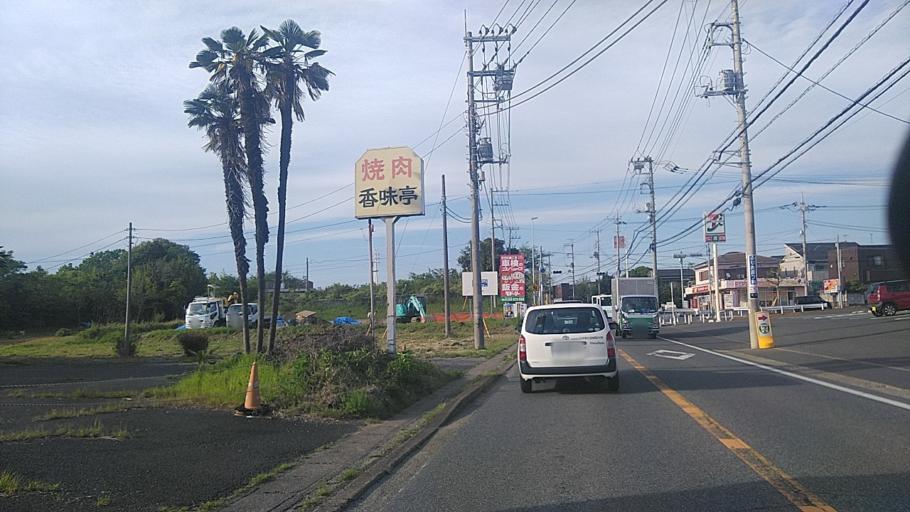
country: JP
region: Chiba
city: Shiroi
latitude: 35.7930
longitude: 140.1327
